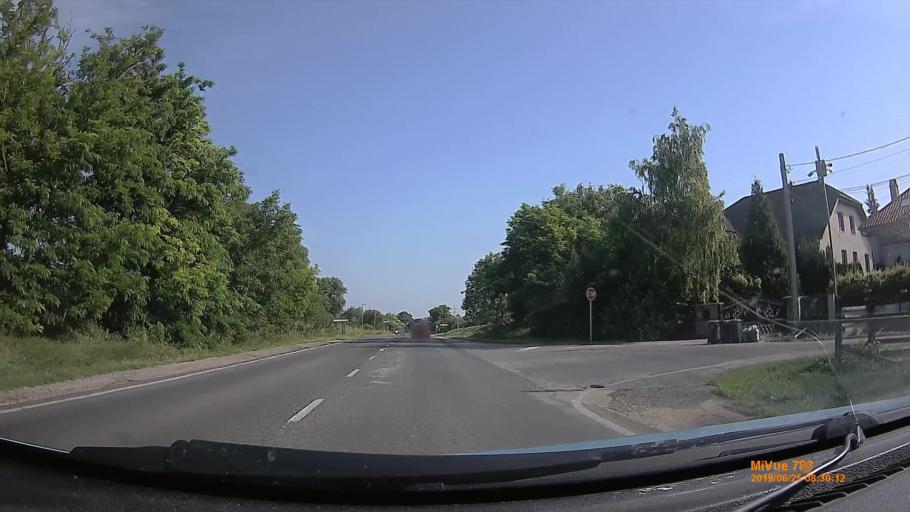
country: HU
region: Fejer
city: Szabadbattyan
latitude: 47.1249
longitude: 18.3764
